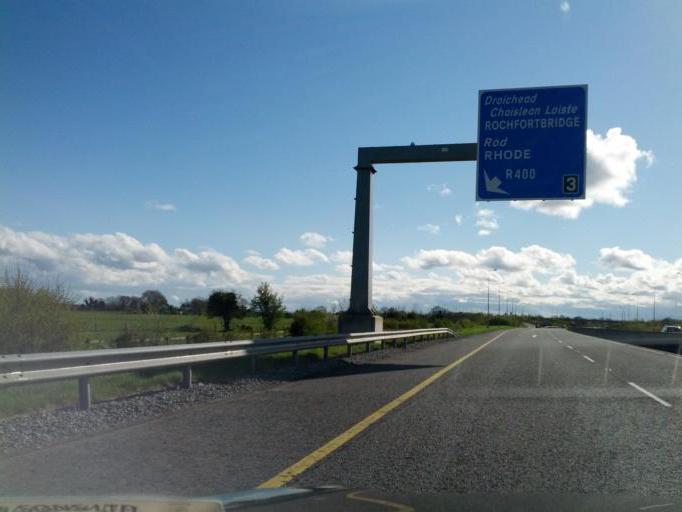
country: IE
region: Leinster
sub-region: An Iarmhi
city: Rochfortbridge
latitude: 53.4086
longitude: -7.2759
